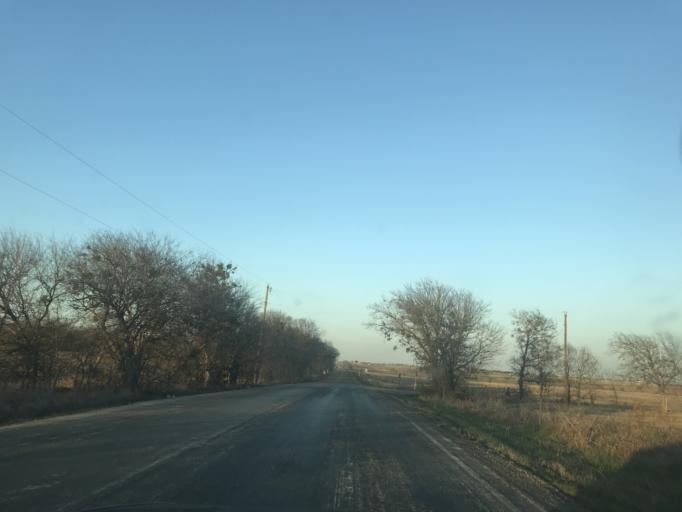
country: US
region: Texas
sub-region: Travis County
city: Pflugerville
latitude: 30.4293
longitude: -97.5303
